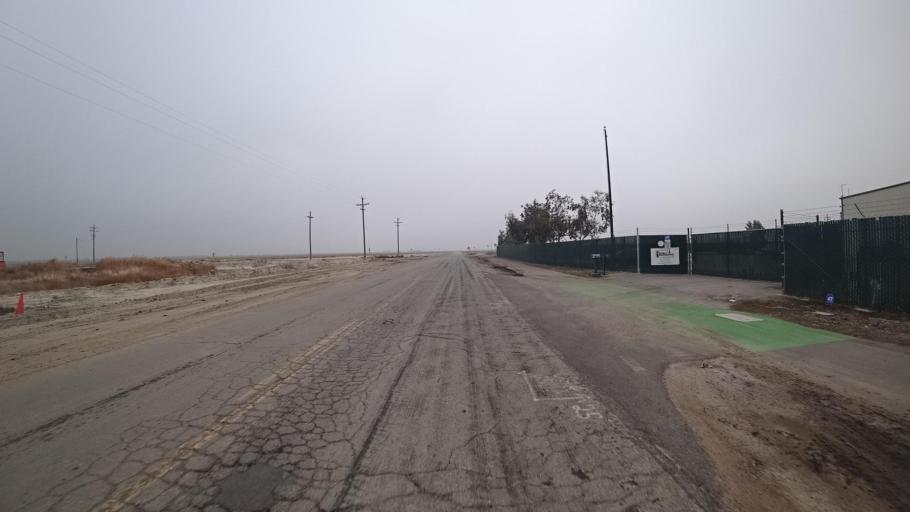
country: US
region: California
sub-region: Kern County
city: Rosedale
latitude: 35.2391
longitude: -119.2529
